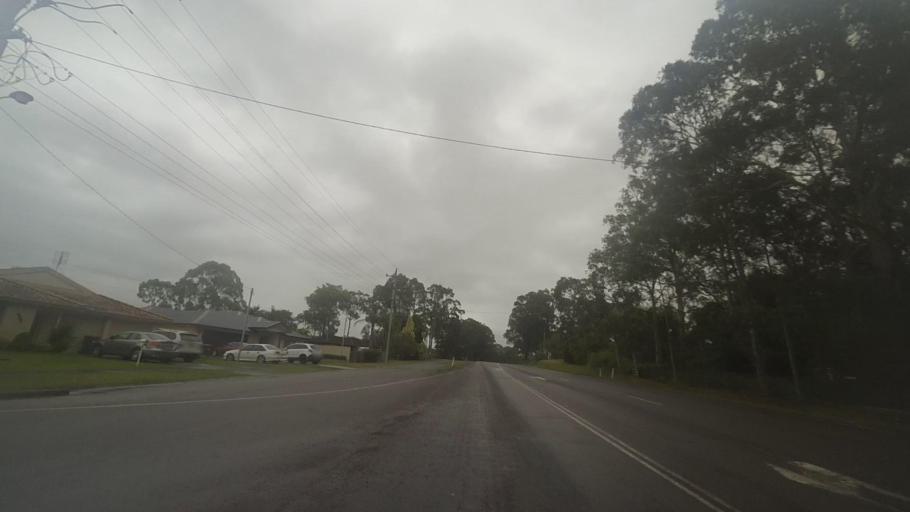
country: AU
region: New South Wales
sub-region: Port Stephens Shire
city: Medowie
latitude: -32.6535
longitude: 151.9558
